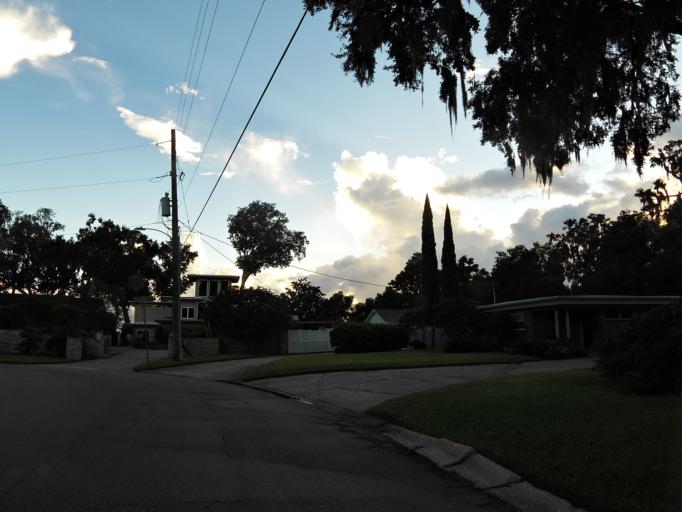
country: US
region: Florida
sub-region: Duval County
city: Jacksonville
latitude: 30.2383
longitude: -81.6264
